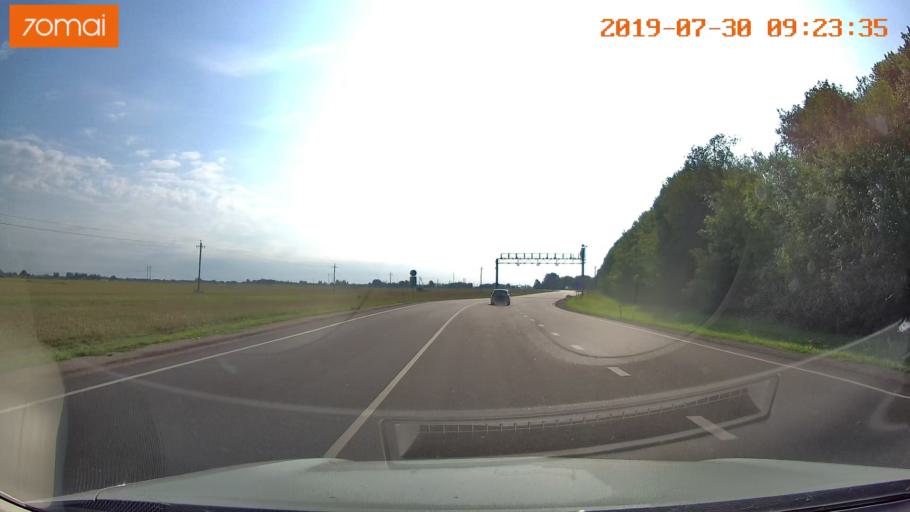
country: LT
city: Kybartai
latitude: 54.6334
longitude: 22.6766
